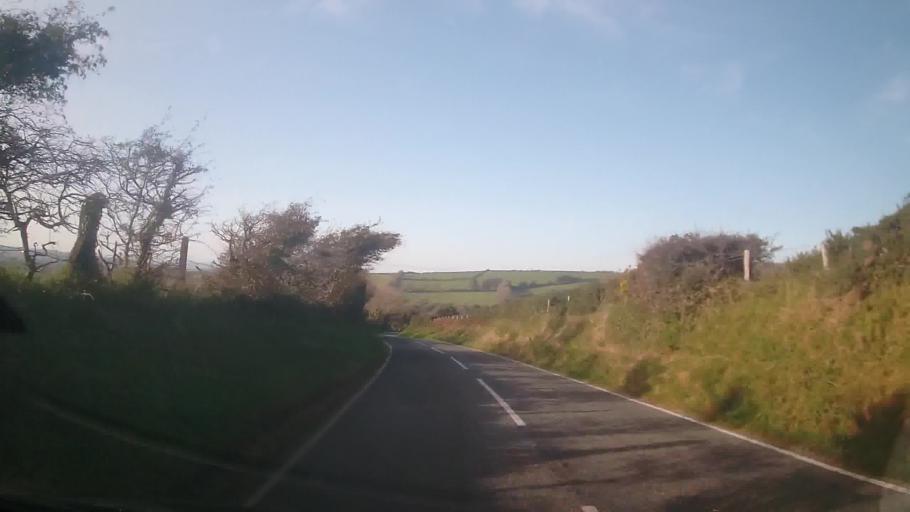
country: GB
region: Wales
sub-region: Pembrokeshire
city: Fishguard
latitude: 51.9739
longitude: -4.9146
